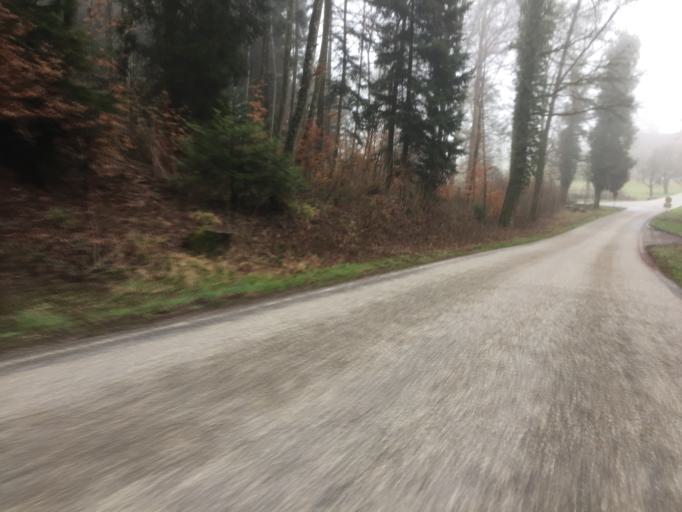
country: CH
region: Bern
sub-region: Seeland District
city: Grossaffoltern
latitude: 47.0904
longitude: 7.3739
